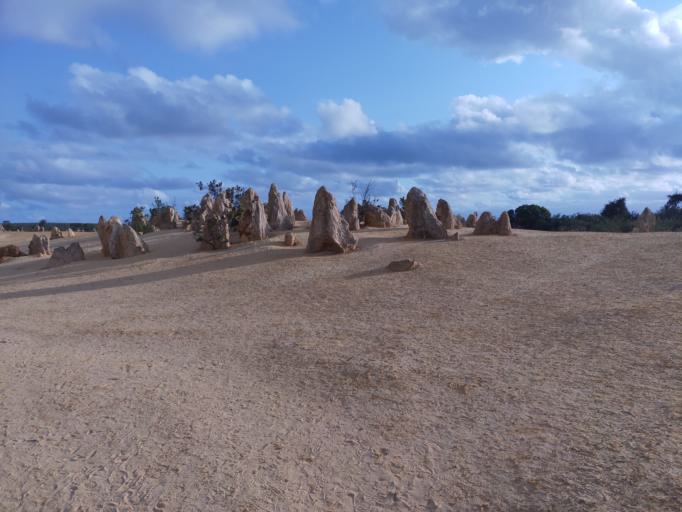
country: AU
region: Western Australia
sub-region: Dandaragan
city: Jurien Bay
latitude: -30.6038
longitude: 115.1502
